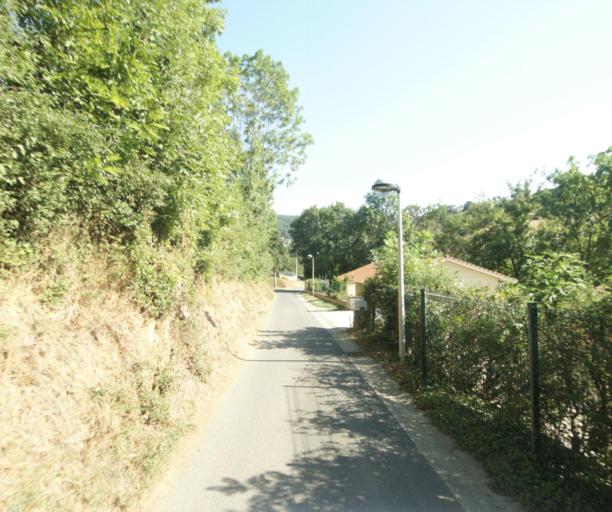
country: FR
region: Rhone-Alpes
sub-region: Departement du Rhone
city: Saint-Pierre-la-Palud
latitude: 45.7867
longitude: 4.6109
